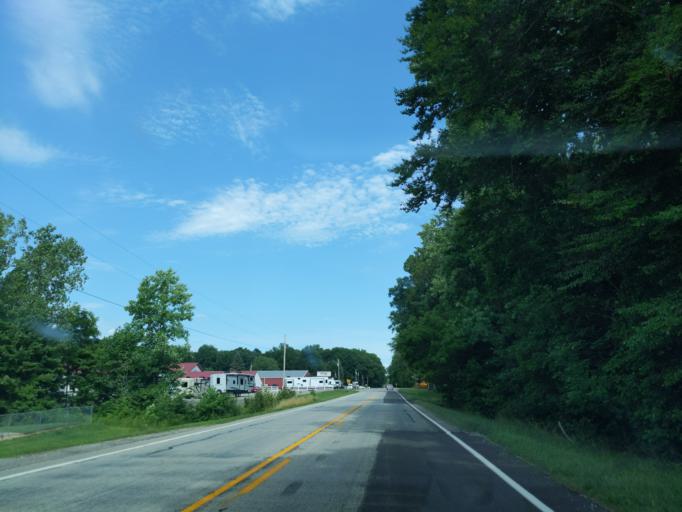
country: US
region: Indiana
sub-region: Ripley County
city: Sunman
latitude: 39.2781
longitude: -85.1306
